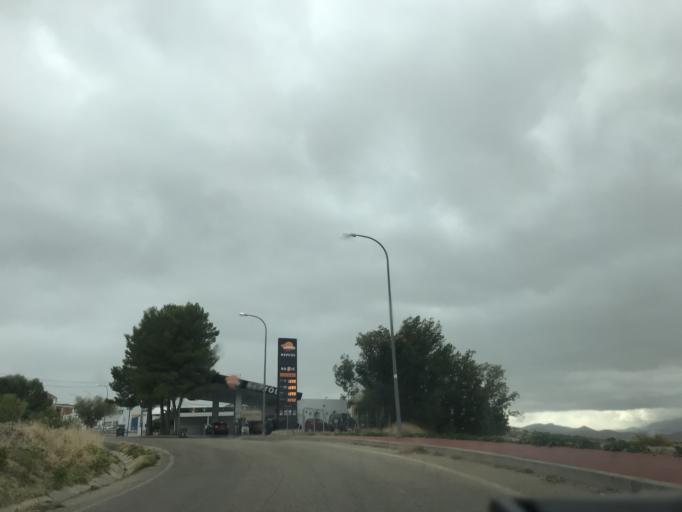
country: ES
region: Andalusia
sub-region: Provincia de Jaen
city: Peal de Becerro
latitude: 37.9165
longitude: -3.1320
